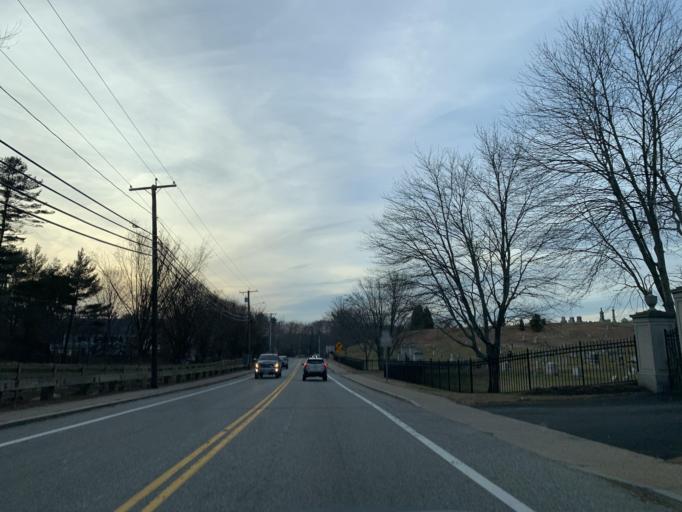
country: US
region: Rhode Island
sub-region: Providence County
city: Chepachet
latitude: 41.9076
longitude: -71.6645
